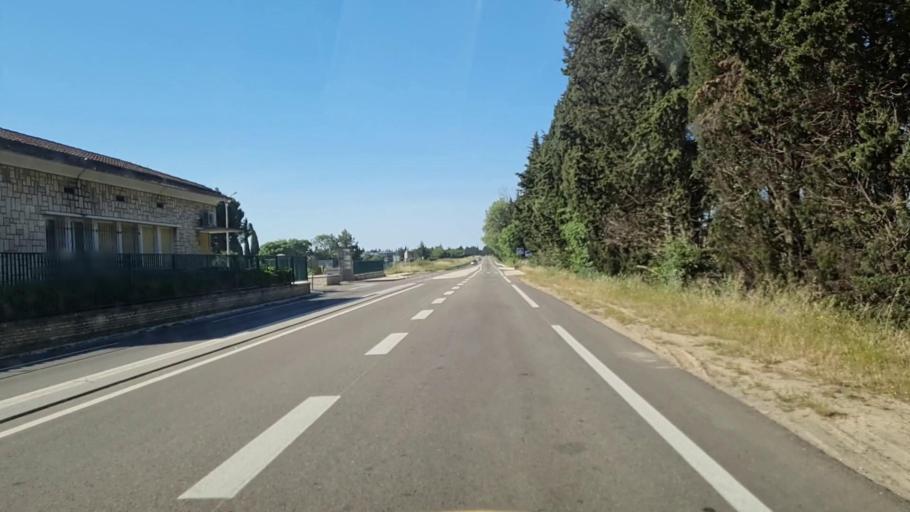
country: FR
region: Languedoc-Roussillon
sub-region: Departement du Gard
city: Garons
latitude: 43.7608
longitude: 4.4059
